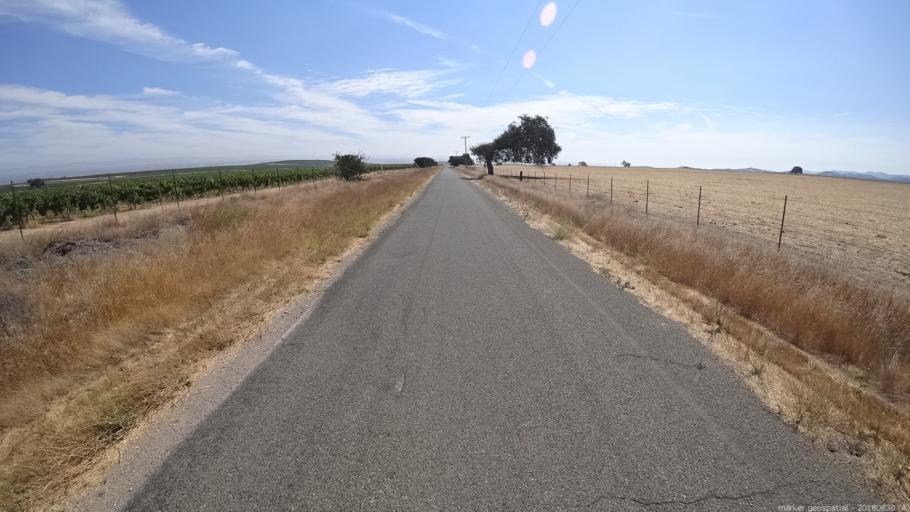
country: US
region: California
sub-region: Monterey County
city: King City
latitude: 36.1109
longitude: -121.0915
